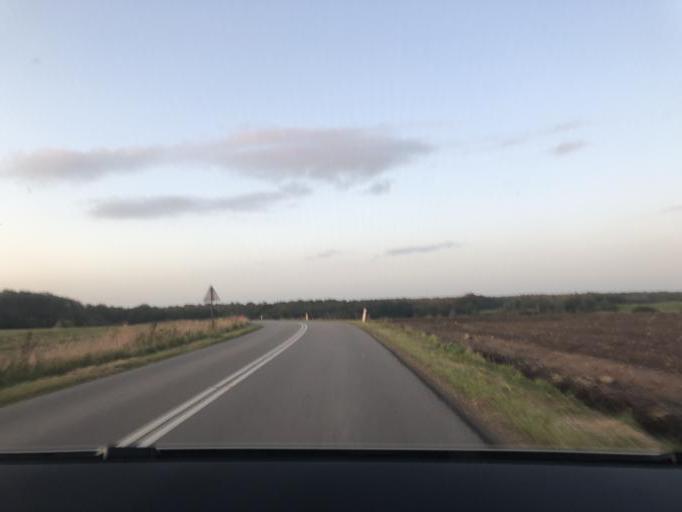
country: DK
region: Capital Region
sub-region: Egedal Kommune
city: Stenlose
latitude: 55.8048
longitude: 12.2120
